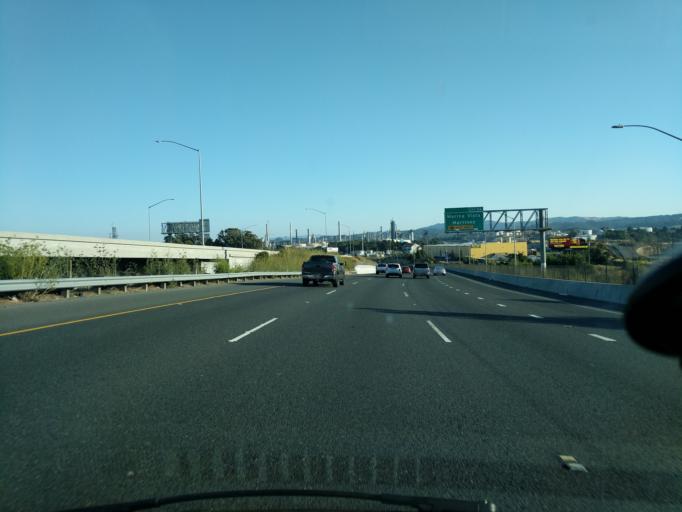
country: US
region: California
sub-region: Contra Costa County
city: Martinez
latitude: 38.0323
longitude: -122.1171
